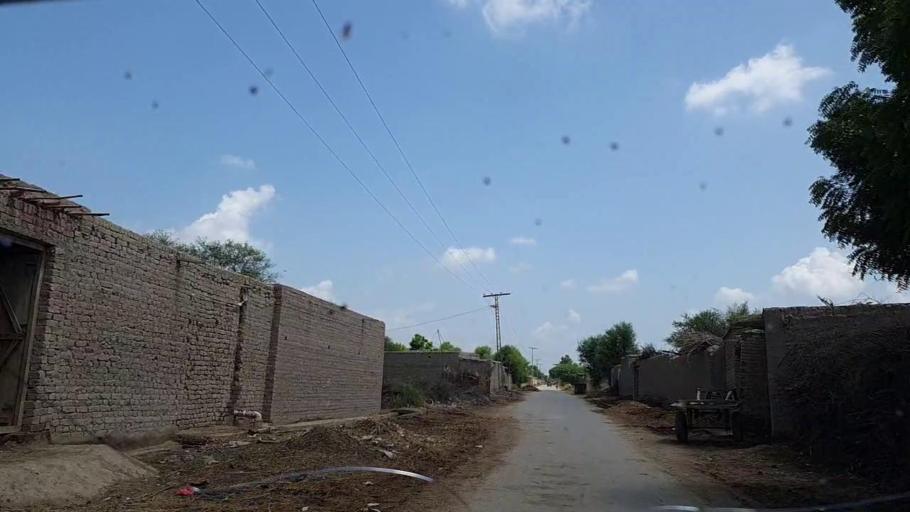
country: PK
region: Sindh
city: Tharu Shah
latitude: 26.9627
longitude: 68.0982
